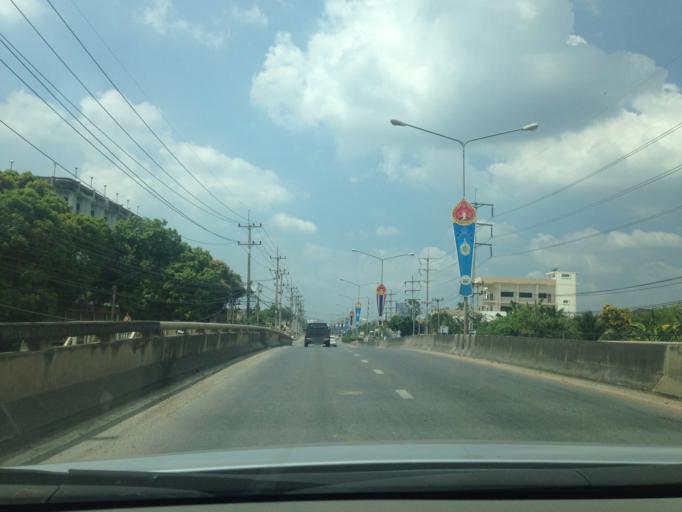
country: TH
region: Pathum Thani
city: Sam Khok
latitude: 14.0683
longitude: 100.5229
